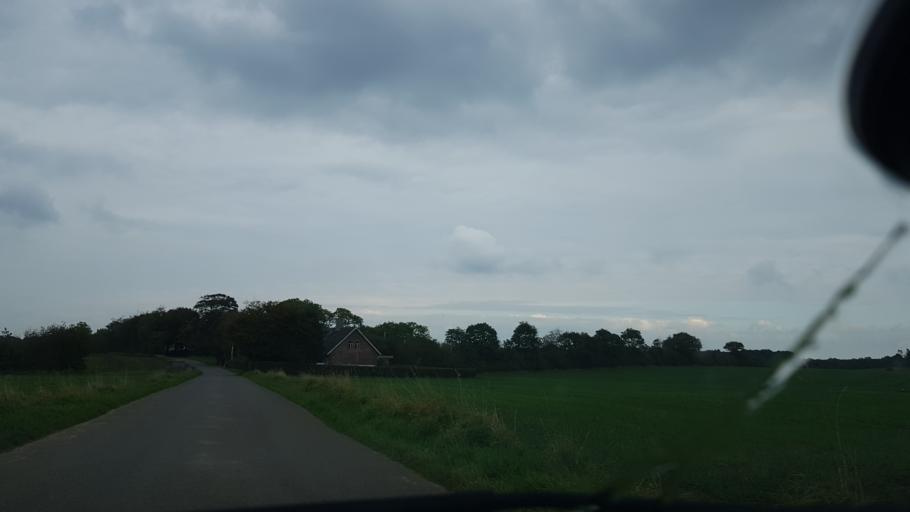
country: DK
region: South Denmark
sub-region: Kolding Kommune
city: Kolding
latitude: 55.5431
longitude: 9.3917
